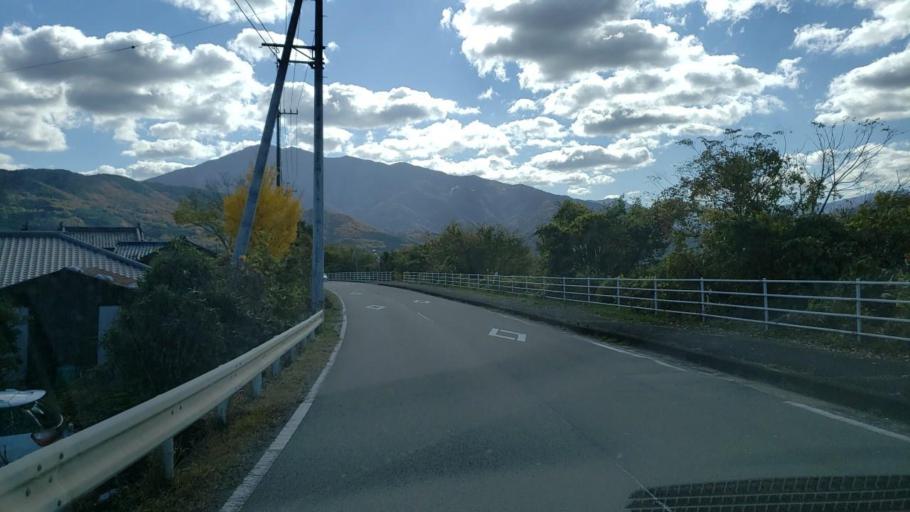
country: JP
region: Tokushima
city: Wakimachi
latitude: 34.0764
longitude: 134.1758
